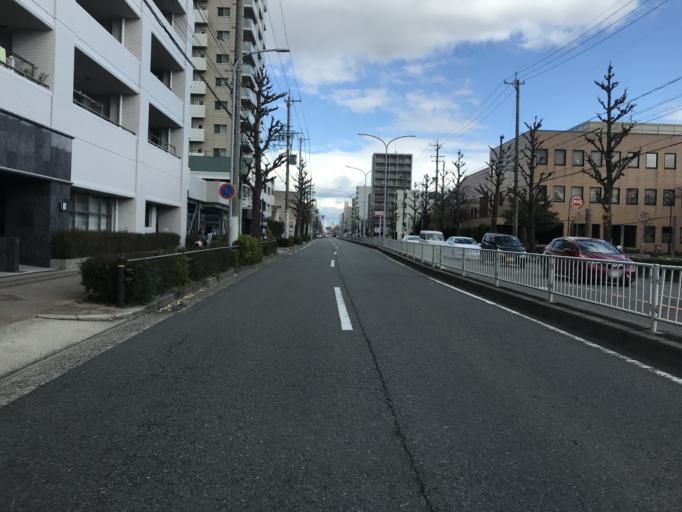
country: JP
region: Aichi
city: Nagoya-shi
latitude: 35.1743
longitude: 136.8639
